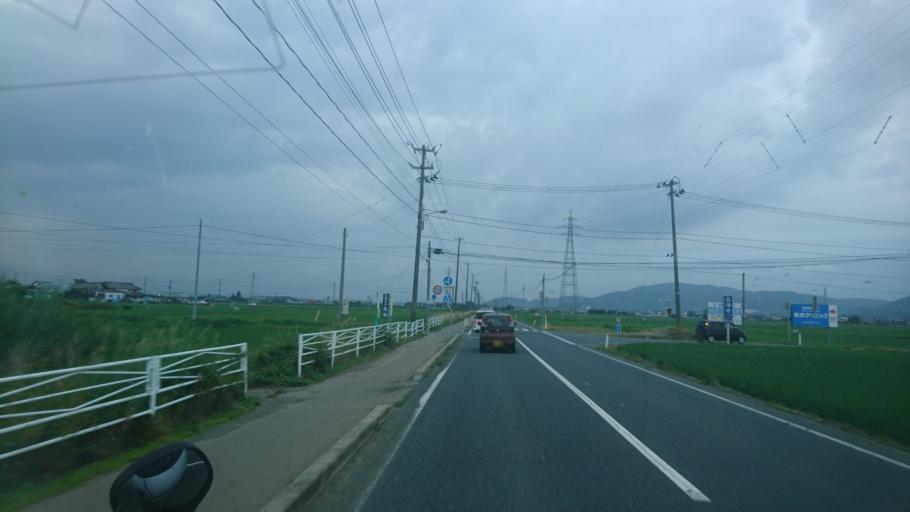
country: JP
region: Iwate
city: Morioka-shi
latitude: 39.6272
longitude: 141.1652
